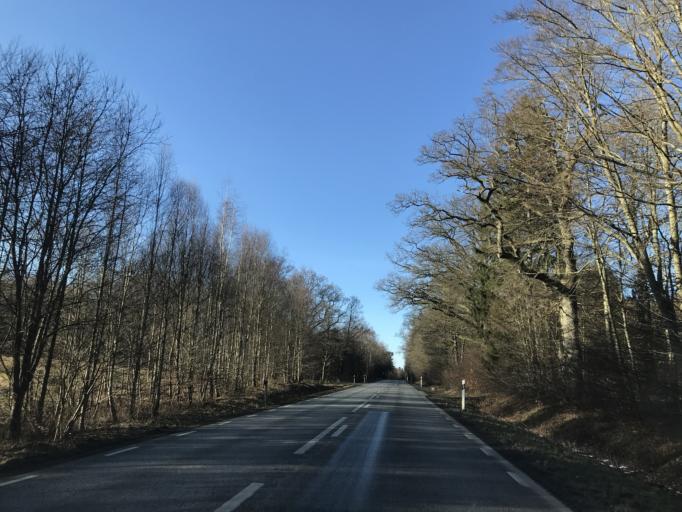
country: SE
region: Skane
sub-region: Sjobo Kommun
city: Sjoebo
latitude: 55.5643
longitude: 13.7453
